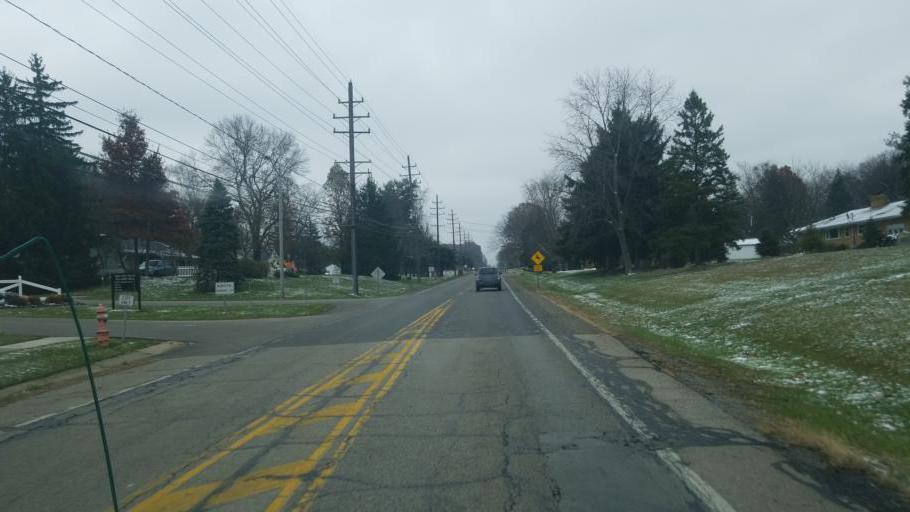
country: US
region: Ohio
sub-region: Cuyahoga County
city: Walton Hills
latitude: 41.3581
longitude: -81.5452
